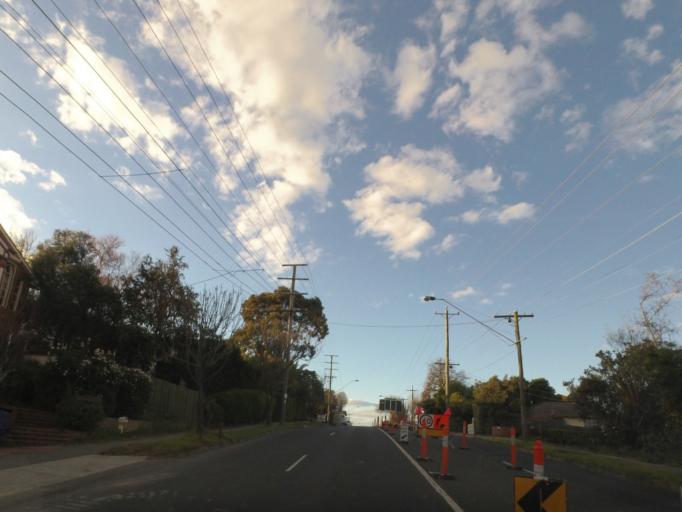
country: AU
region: Victoria
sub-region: Whitehorse
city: Surrey Hills
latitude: -37.8290
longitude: 145.0994
